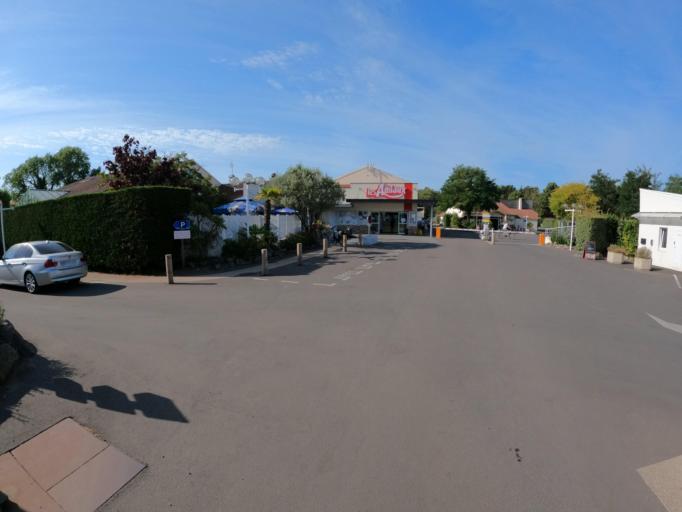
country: FR
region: Pays de la Loire
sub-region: Departement de la Vendee
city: Saint-Jean-de-Monts
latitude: 46.8080
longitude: -2.1047
